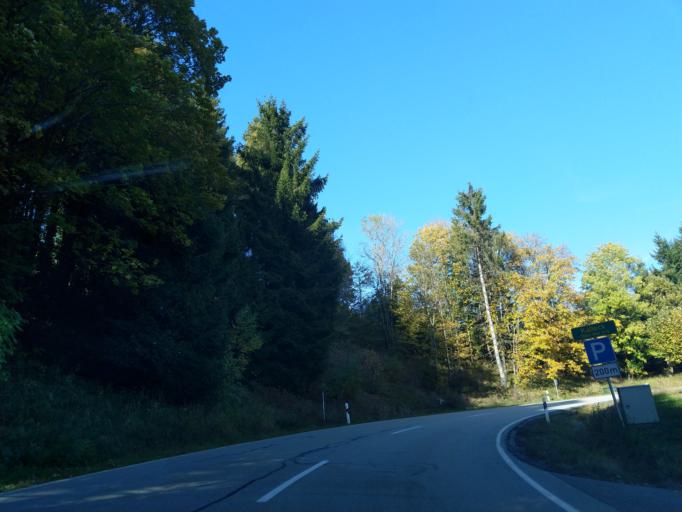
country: DE
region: Bavaria
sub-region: Lower Bavaria
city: Bobrach
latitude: 48.9388
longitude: 12.9176
